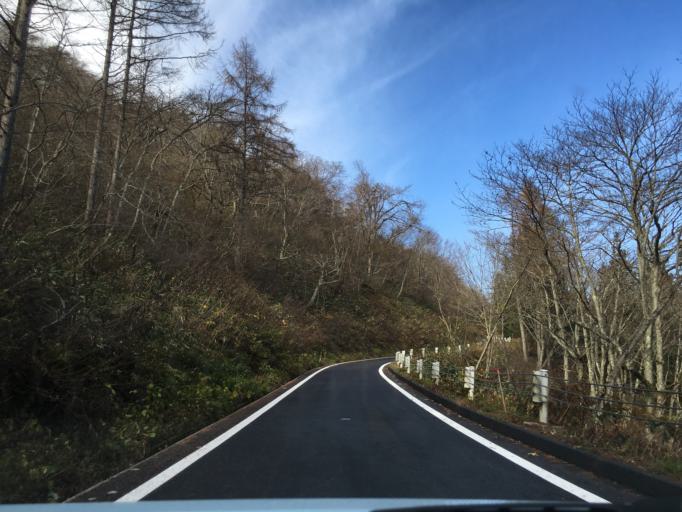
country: JP
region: Fukushima
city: Inawashiro
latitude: 37.4568
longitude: 139.9956
